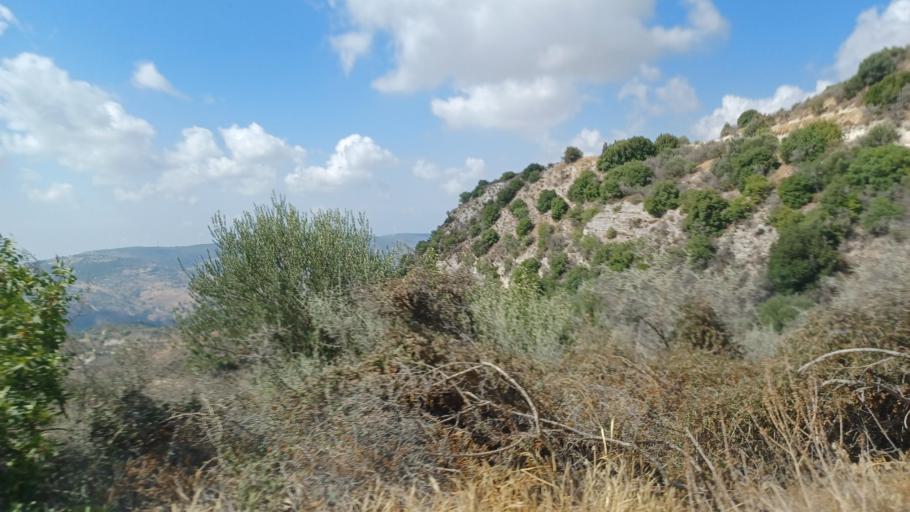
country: CY
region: Limassol
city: Pachna
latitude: 34.8006
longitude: 32.6669
